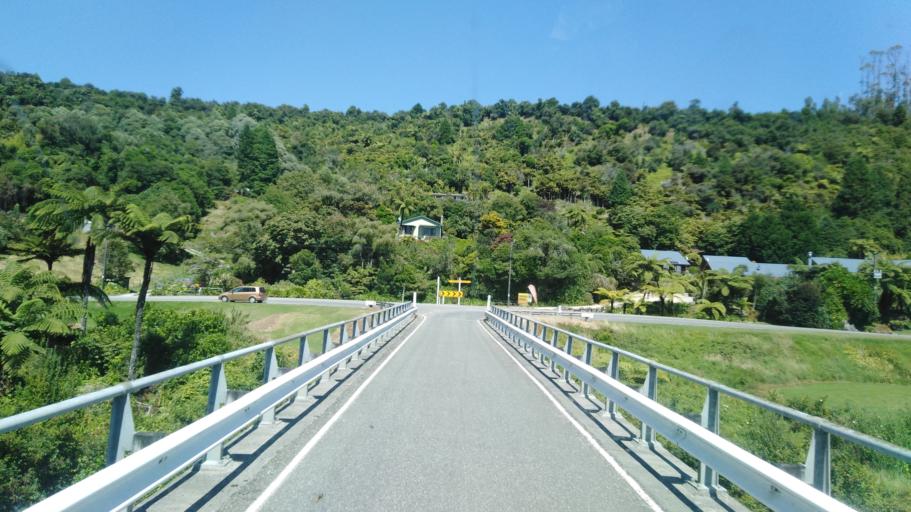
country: NZ
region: West Coast
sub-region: Buller District
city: Westport
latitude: -41.2613
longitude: 172.1309
